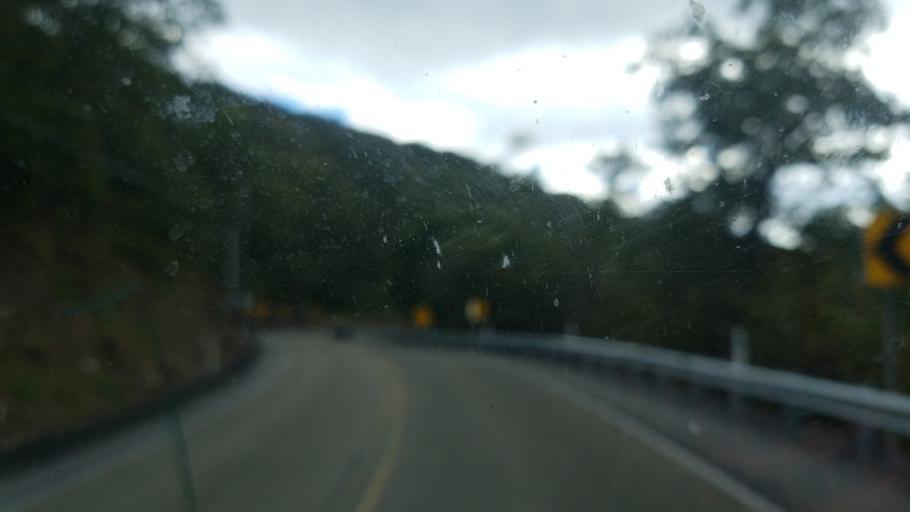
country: US
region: Pennsylvania
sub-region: Fulton County
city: McConnellsburg
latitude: 39.9236
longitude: -77.9605
